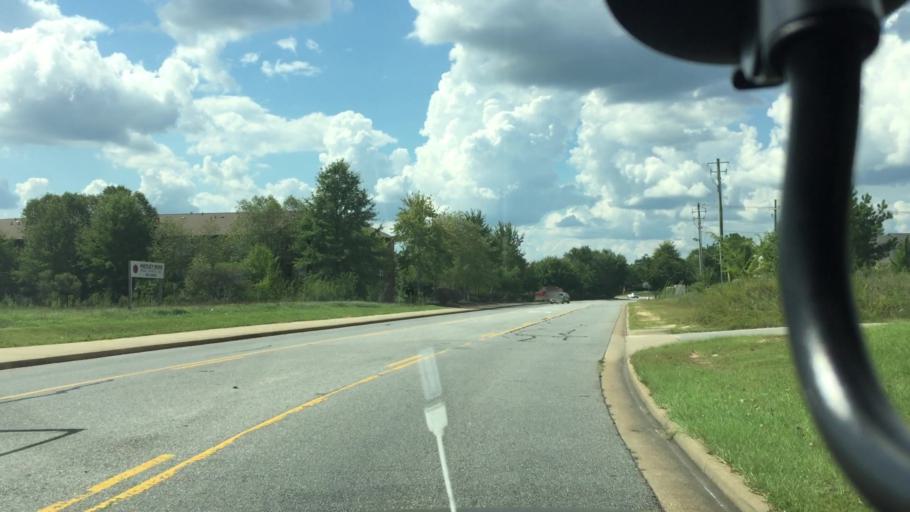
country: US
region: Alabama
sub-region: Lee County
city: Auburn
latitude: 32.5734
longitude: -85.5010
